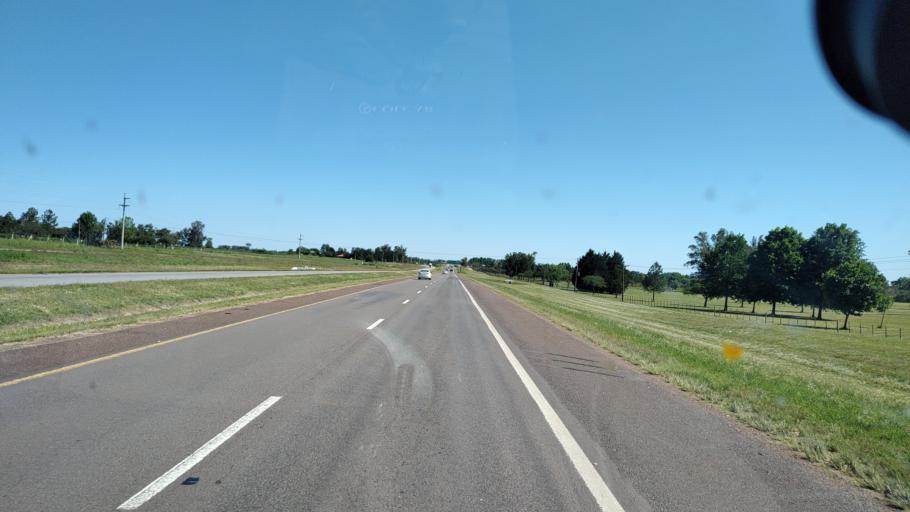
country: UY
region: Paysandu
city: San Felix
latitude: -32.3223
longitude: -58.2577
